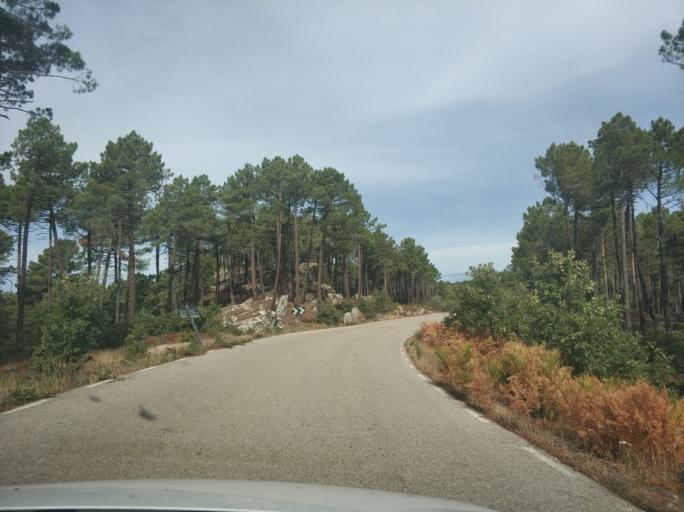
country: ES
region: Castille and Leon
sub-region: Provincia de Soria
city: Duruelo de la Sierra
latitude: 41.8874
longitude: -2.9395
